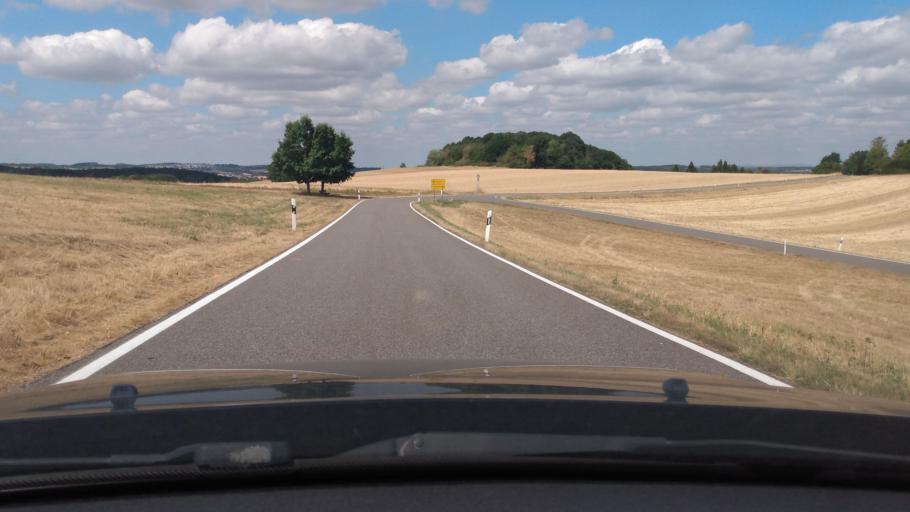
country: DE
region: Rheinland-Pfalz
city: Kommen
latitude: 49.8943
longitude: 7.1564
